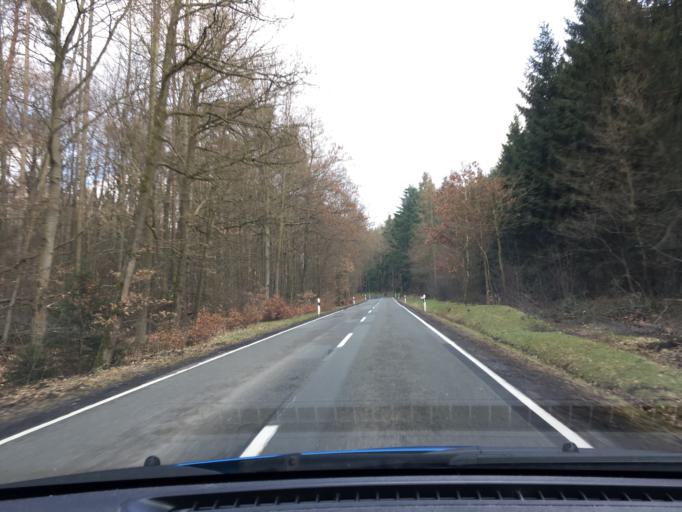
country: DE
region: Lower Saxony
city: Uslar
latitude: 51.5900
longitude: 9.6243
